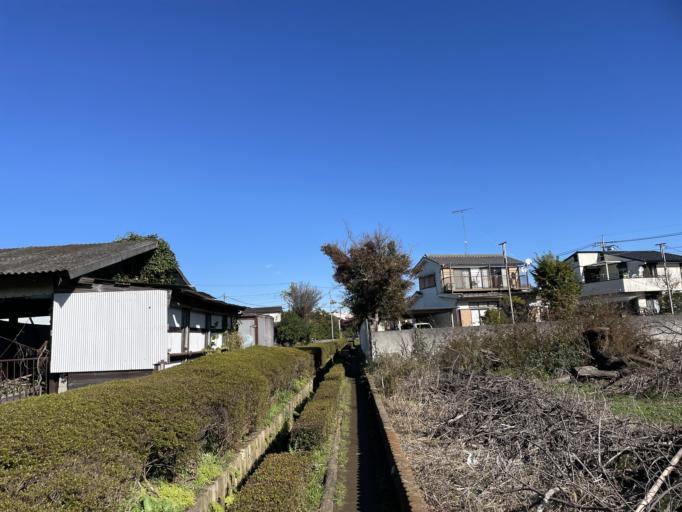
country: JP
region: Tokyo
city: Tanashicho
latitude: 35.7787
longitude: 139.5516
